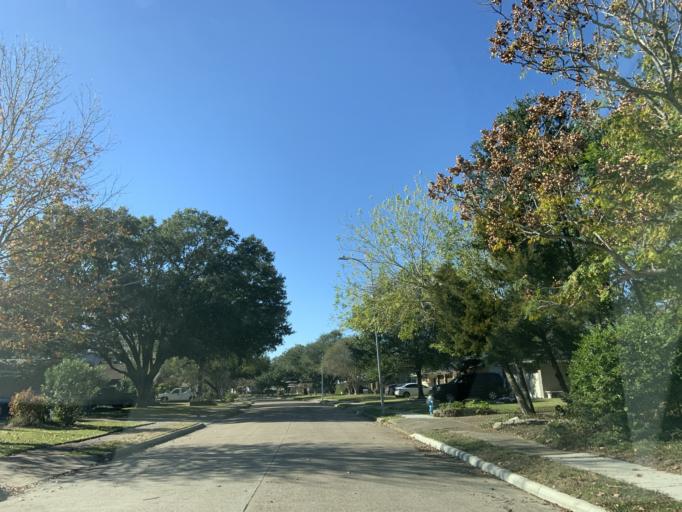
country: US
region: Texas
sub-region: Harris County
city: Bellaire
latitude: 29.6956
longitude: -95.5072
